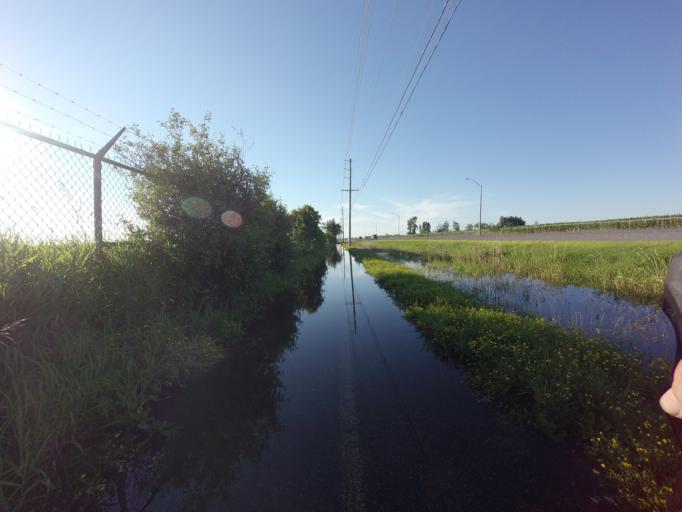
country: CA
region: Ontario
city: Bells Corners
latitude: 45.2987
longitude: -75.7635
